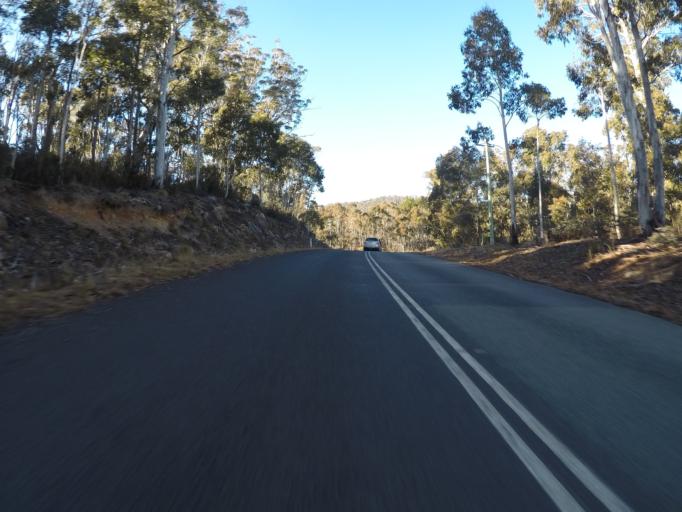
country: AU
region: Australian Capital Territory
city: Macarthur
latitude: -35.5085
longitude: 148.9283
